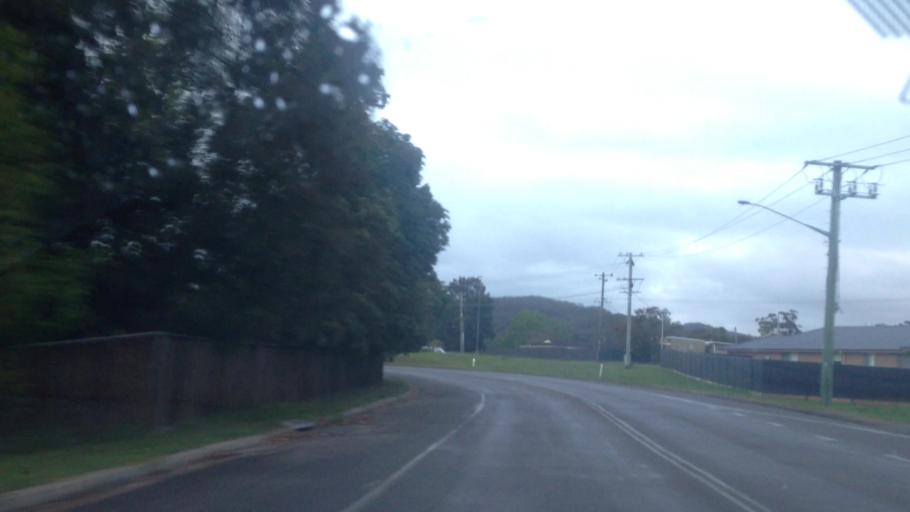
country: AU
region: New South Wales
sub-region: Lake Macquarie Shire
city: Cooranbong
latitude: -33.0797
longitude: 151.4473
